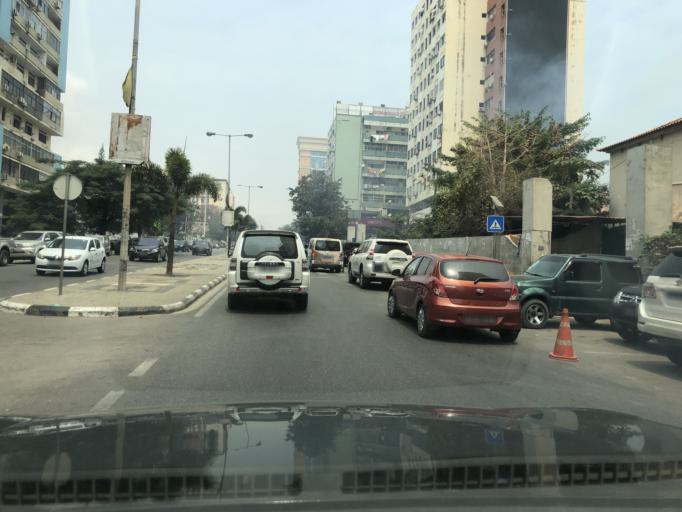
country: AO
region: Luanda
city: Luanda
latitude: -8.8182
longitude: 13.2291
